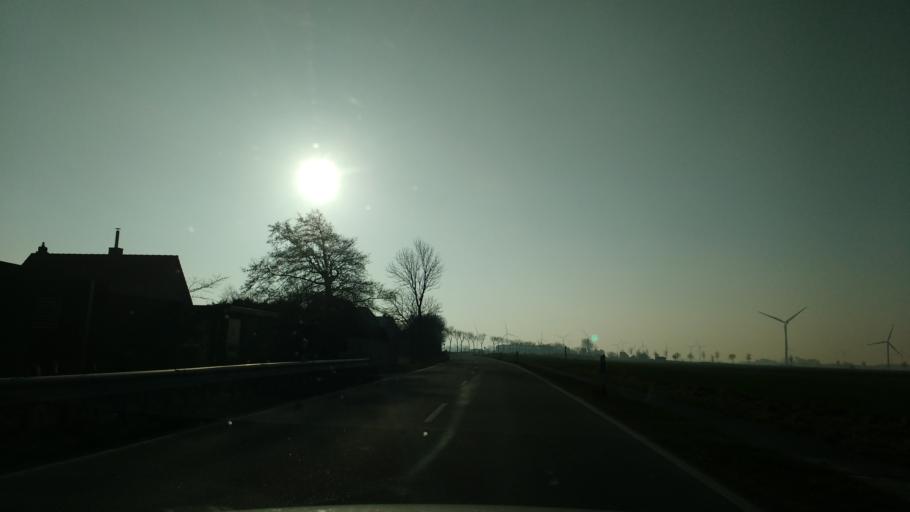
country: DE
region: Schleswig-Holstein
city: Helse
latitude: 53.9897
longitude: 8.9947
